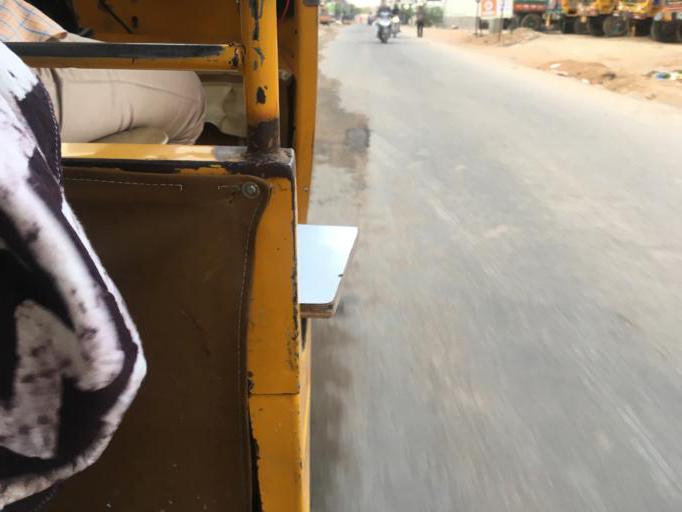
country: IN
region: Telangana
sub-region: Medak
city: Serilingampalle
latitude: 17.4328
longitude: 78.3340
